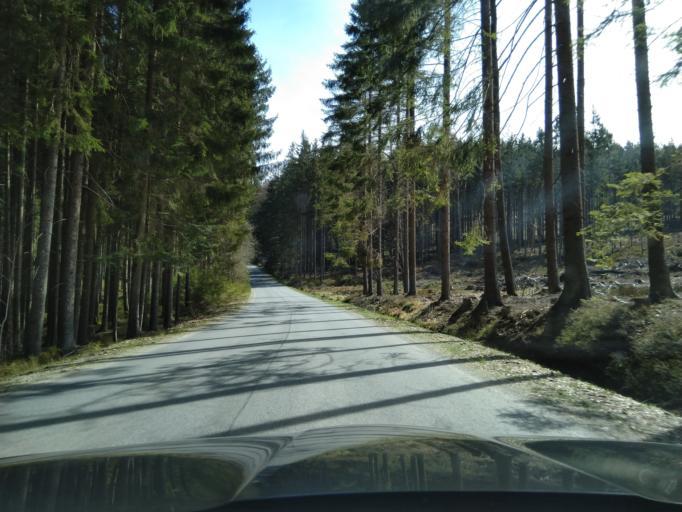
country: CZ
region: Jihocesky
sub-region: Okres Prachatice
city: Stachy
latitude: 49.0736
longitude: 13.6428
